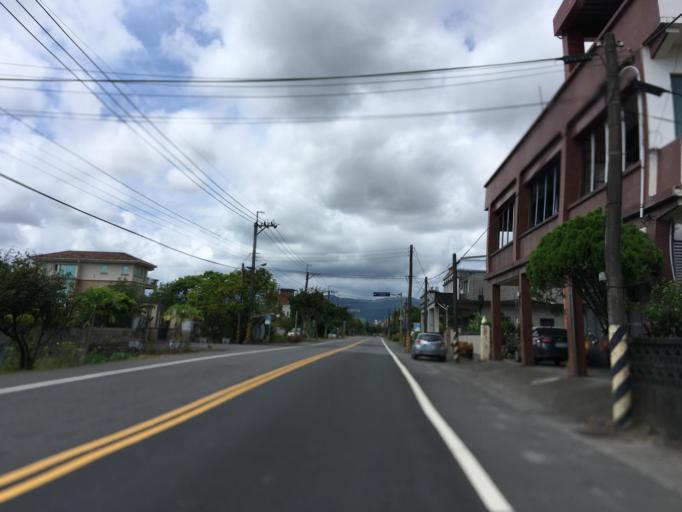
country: TW
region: Taiwan
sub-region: Yilan
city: Yilan
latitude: 24.6977
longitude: 121.7350
